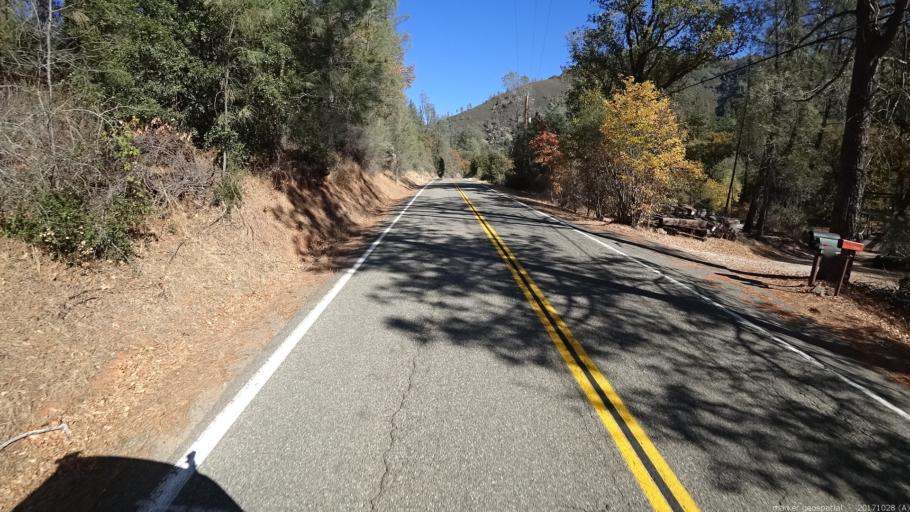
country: US
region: California
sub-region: Trinity County
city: Lewiston
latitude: 40.7246
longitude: -122.6262
